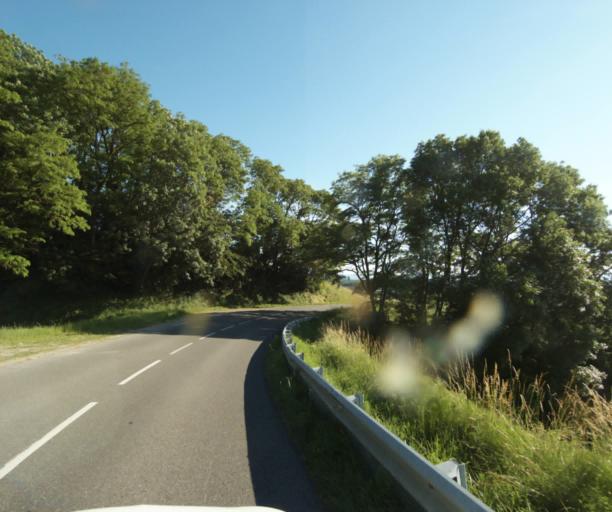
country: FR
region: Rhone-Alpes
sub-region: Departement de la Haute-Savoie
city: Loisin
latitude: 46.2927
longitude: 6.3178
